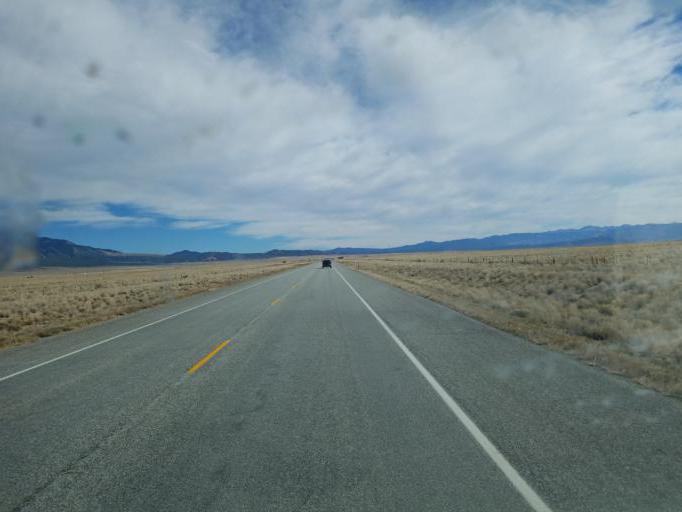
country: US
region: Colorado
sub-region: Alamosa County
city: Alamosa East
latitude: 37.4750
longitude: -105.6249
